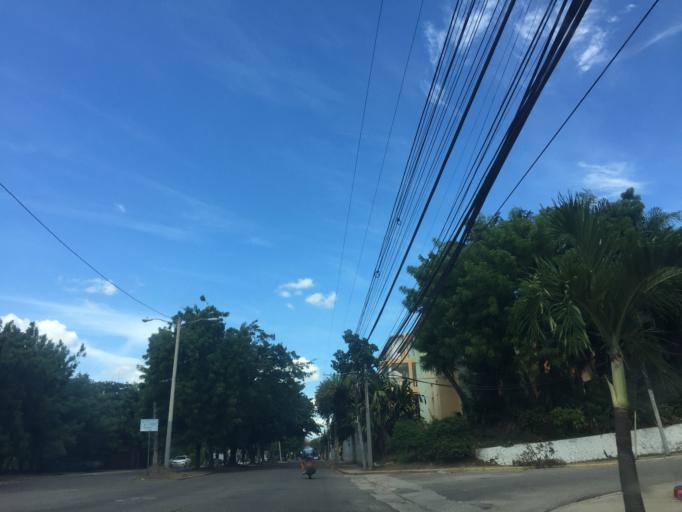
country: DO
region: Santiago
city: Santiago de los Caballeros
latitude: 19.4355
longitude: -70.6845
